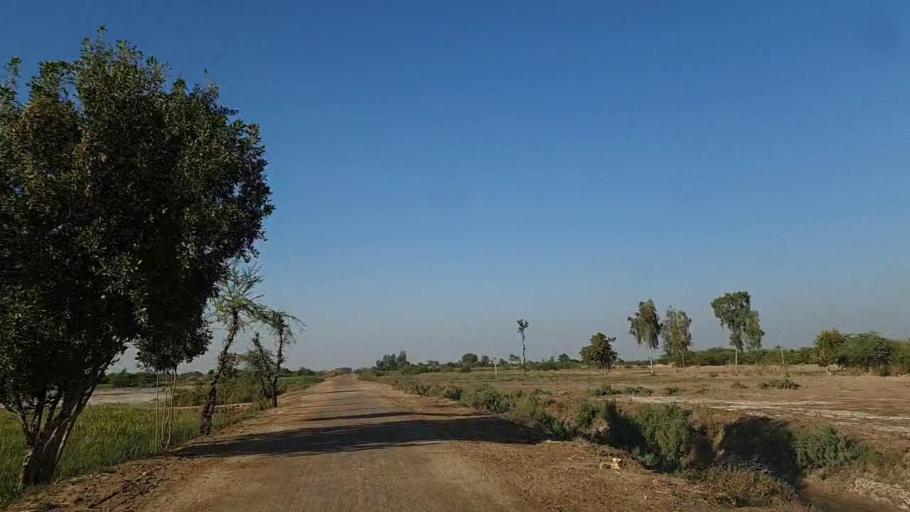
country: PK
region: Sindh
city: Samaro
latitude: 25.3452
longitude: 69.3674
